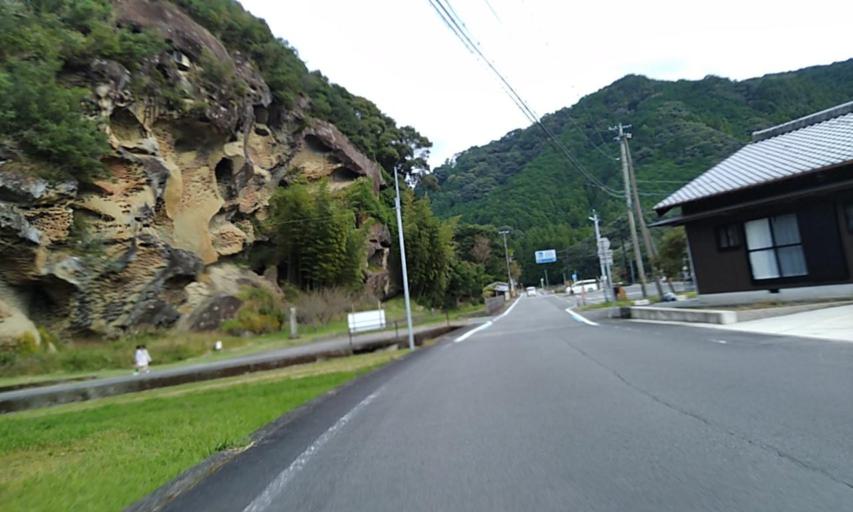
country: JP
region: Wakayama
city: Shingu
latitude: 33.5397
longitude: 135.8255
